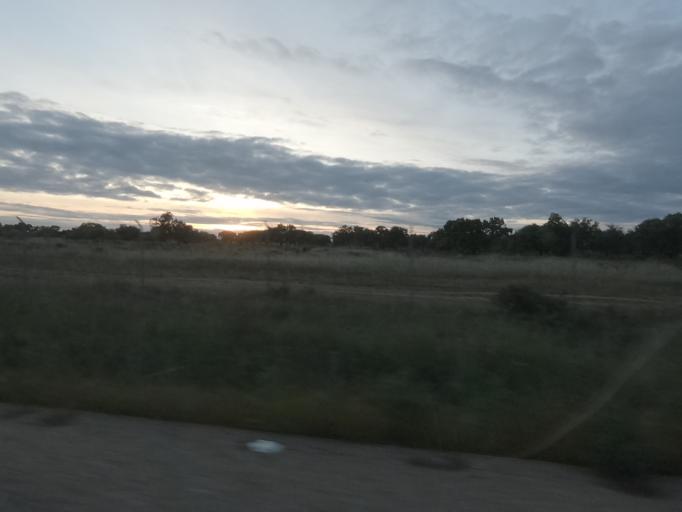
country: ES
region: Extremadura
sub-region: Provincia de Badajoz
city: Villar del Rey
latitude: 38.9953
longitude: -6.8705
